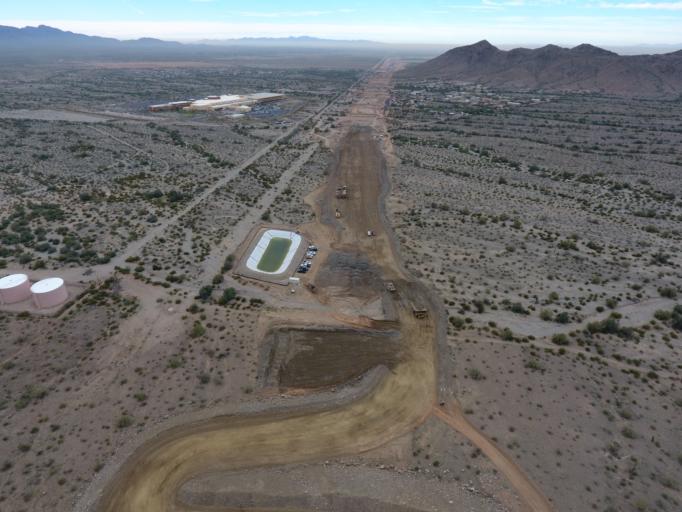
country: US
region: Arizona
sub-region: Maricopa County
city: Laveen
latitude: 33.3055
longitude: -112.1463
